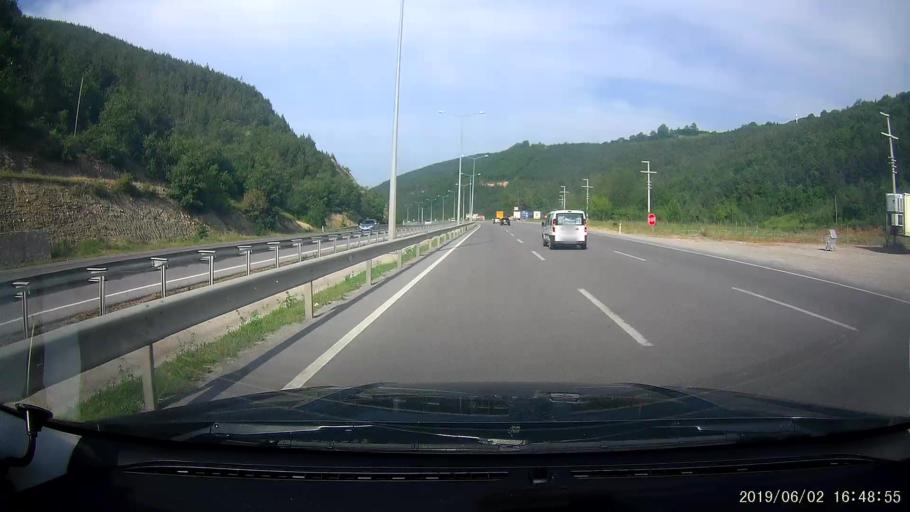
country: TR
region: Samsun
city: Taflan
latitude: 41.2317
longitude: 36.1494
